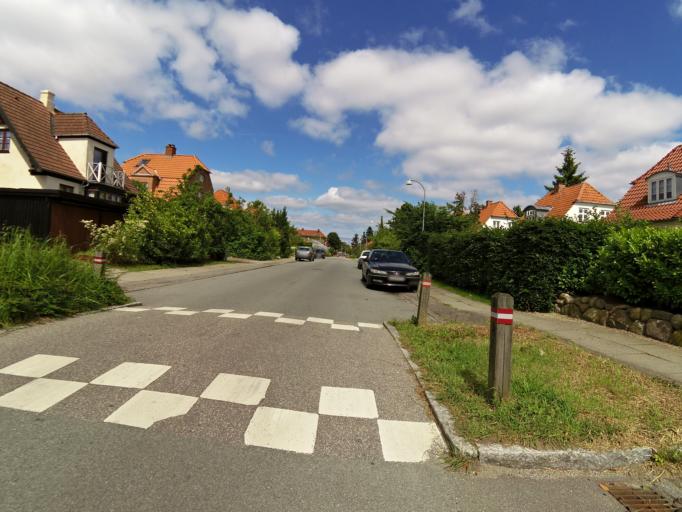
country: DK
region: Capital Region
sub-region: Gladsaxe Municipality
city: Buddinge
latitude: 55.7323
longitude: 12.5104
